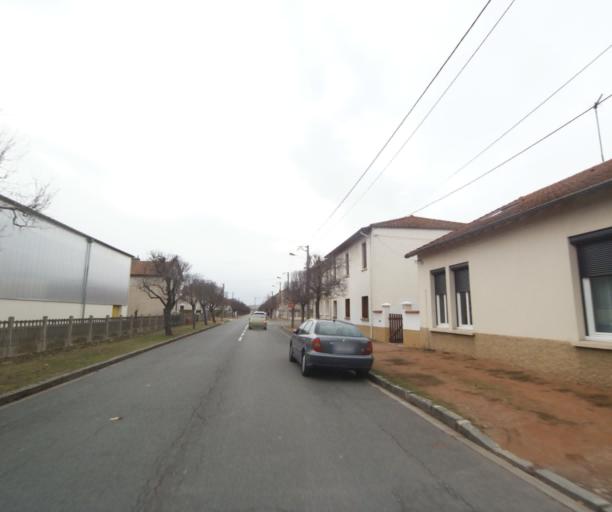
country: FR
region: Rhone-Alpes
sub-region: Departement de la Loire
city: Le Coteau
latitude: 46.0536
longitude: 4.0920
